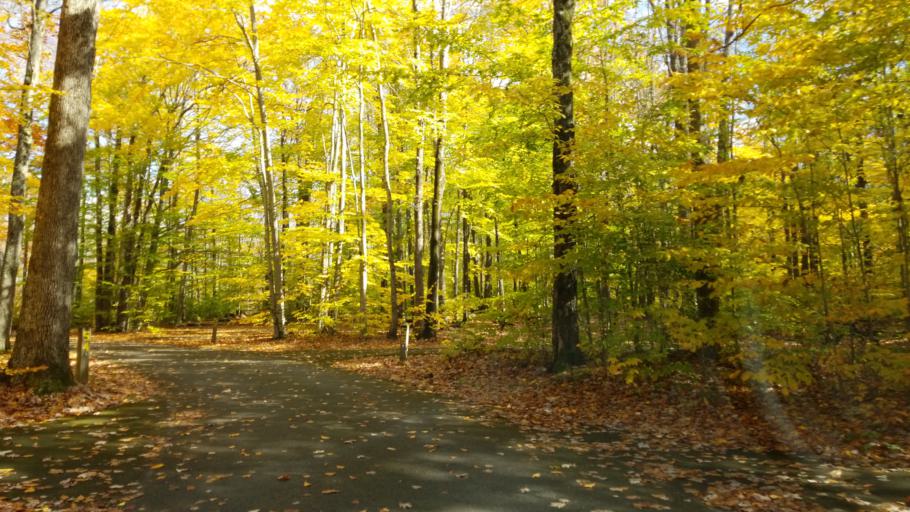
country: US
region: Pennsylvania
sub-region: Clearfield County
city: Clearfield
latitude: 41.1959
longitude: -78.5038
